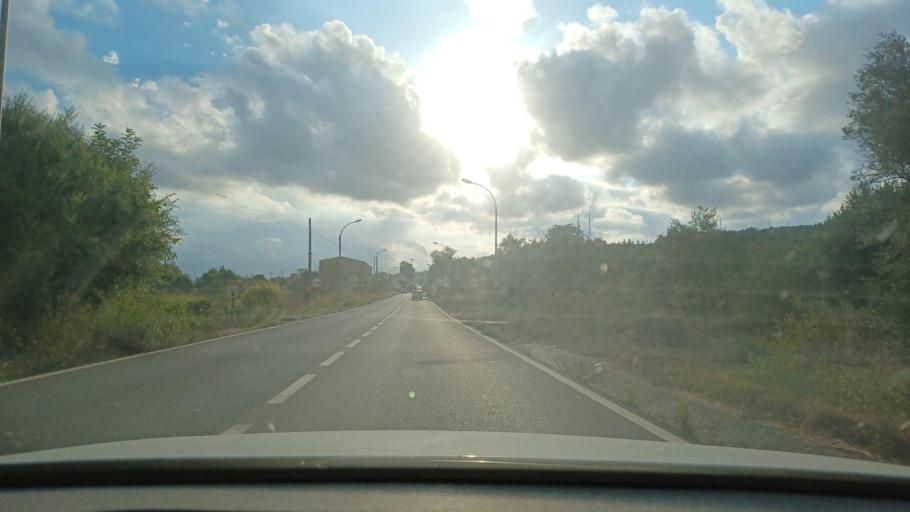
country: ES
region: Catalonia
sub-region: Provincia de Tarragona
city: Alcanar
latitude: 40.5450
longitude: 0.4932
